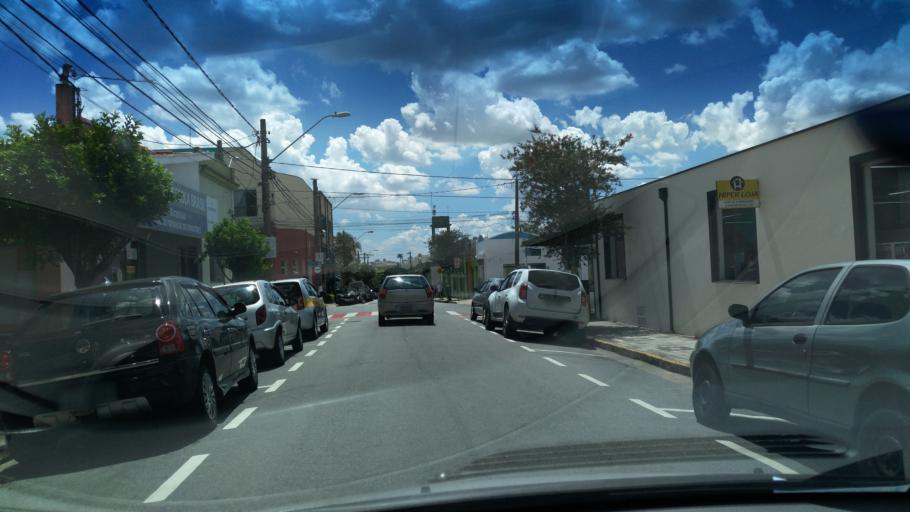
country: BR
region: Sao Paulo
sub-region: Vinhedo
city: Vinhedo
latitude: -23.0289
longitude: -46.9728
